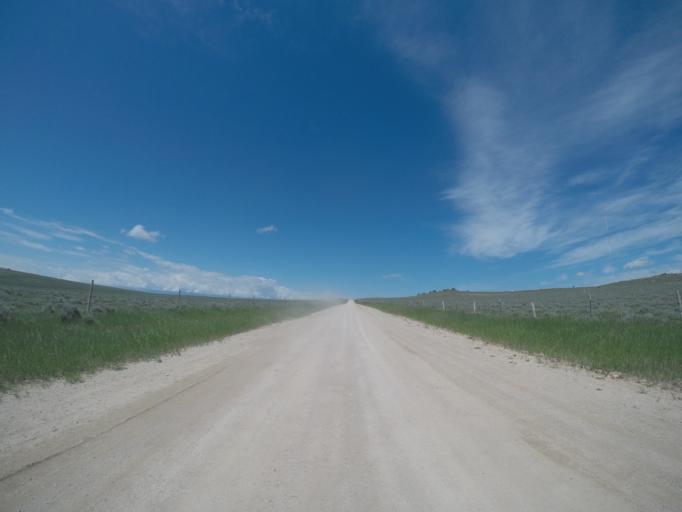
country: US
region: Wyoming
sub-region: Park County
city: Powell
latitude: 45.2052
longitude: -108.7603
